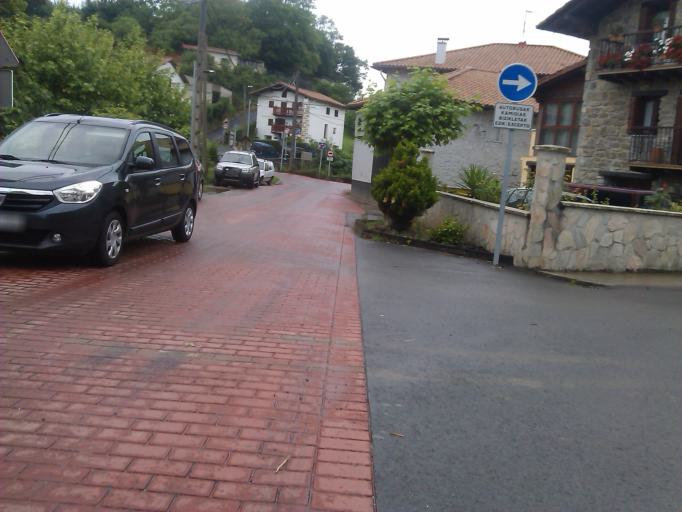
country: ES
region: Basque Country
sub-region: Provincia de Guipuzcoa
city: Hernani
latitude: 43.2629
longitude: -1.9731
